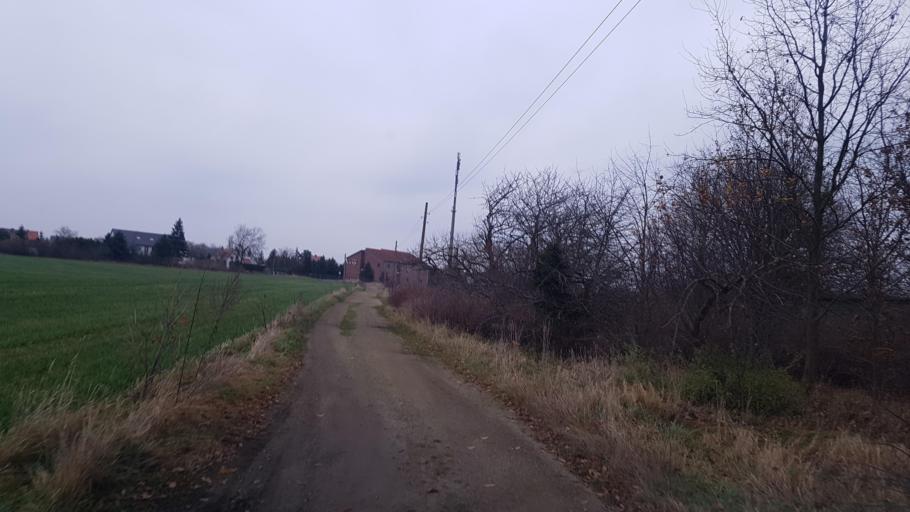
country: DE
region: Brandenburg
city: Tettau
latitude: 51.4683
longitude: 13.7308
